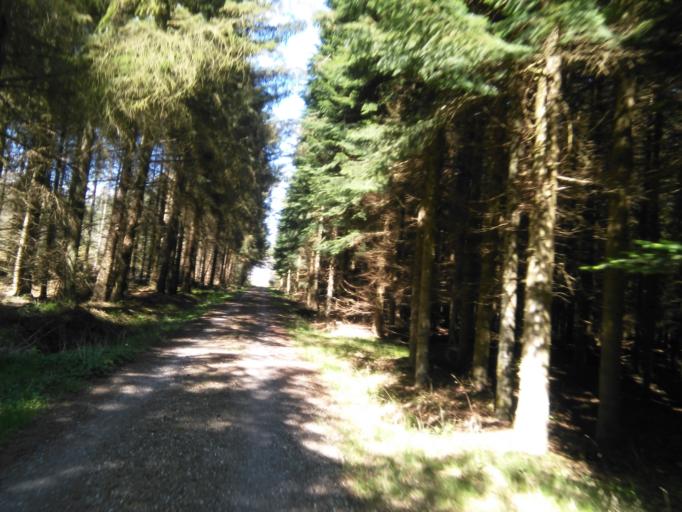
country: DK
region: Central Jutland
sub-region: Hedensted Kommune
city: Juelsminde
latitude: 55.7501
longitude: 10.0768
